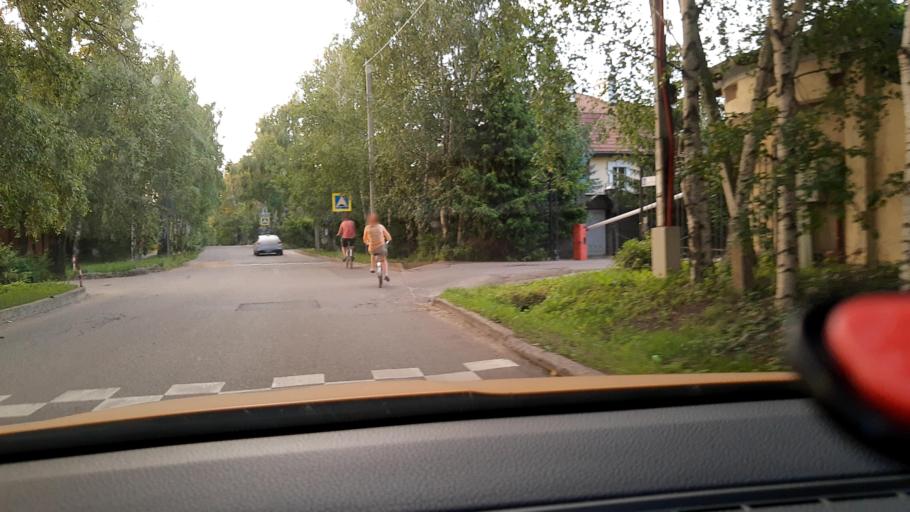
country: RU
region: Moskovskaya
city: Barvikha
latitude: 55.7291
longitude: 37.2903
